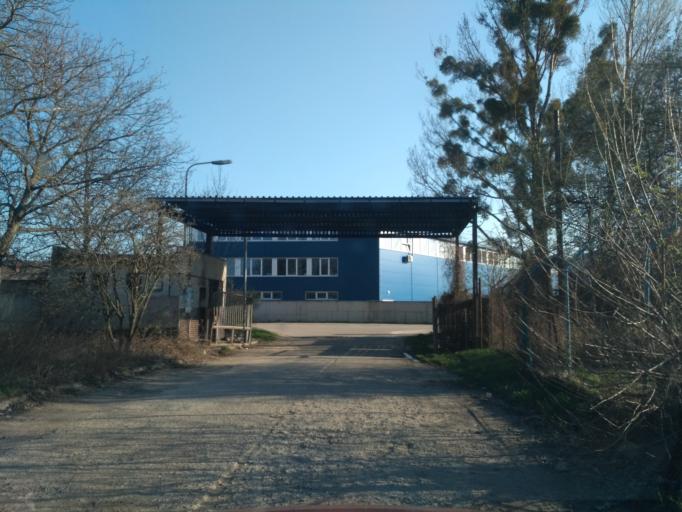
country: SK
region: Kosicky
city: Kosice
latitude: 48.6722
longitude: 21.2964
